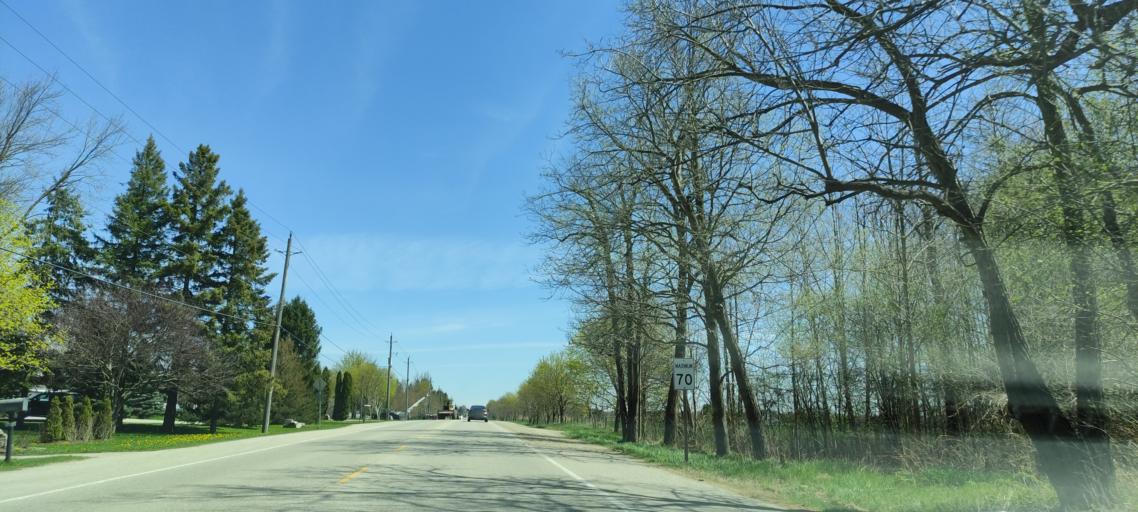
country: CA
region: Ontario
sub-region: Wellington County
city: Guelph
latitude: 43.5970
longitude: -80.3402
